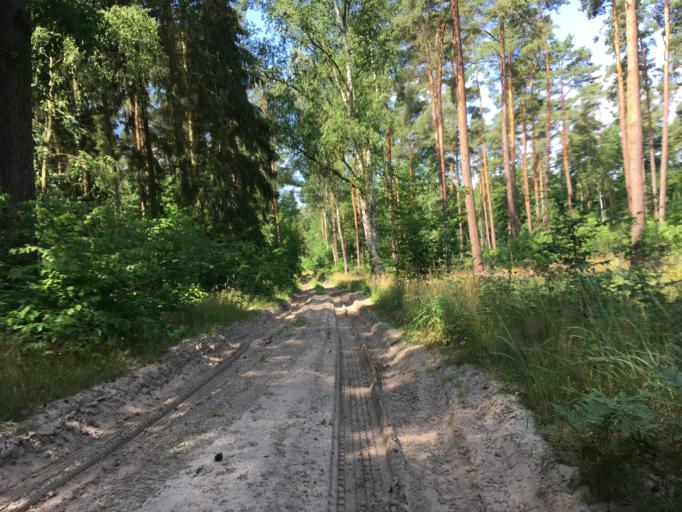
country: DE
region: Brandenburg
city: Casekow
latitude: 53.2308
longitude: 14.1275
